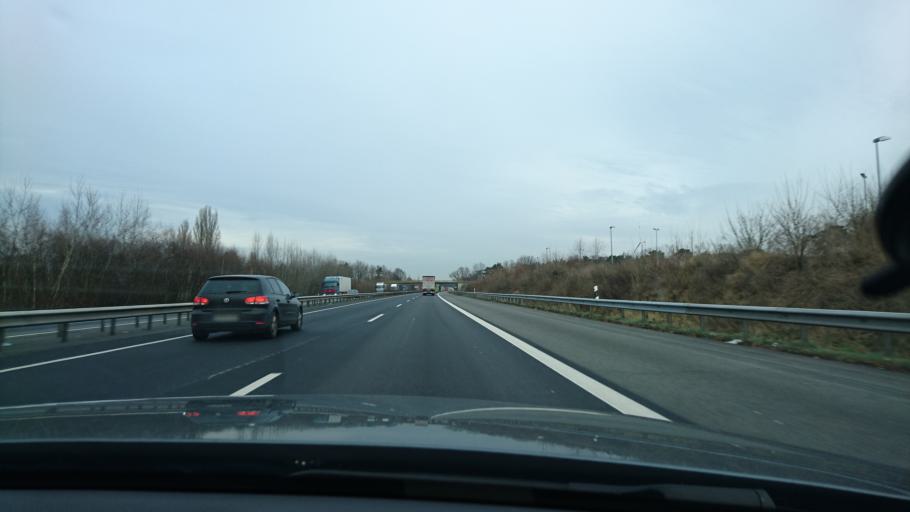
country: DE
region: Lower Saxony
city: Bramsche
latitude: 52.4131
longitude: 8.0317
